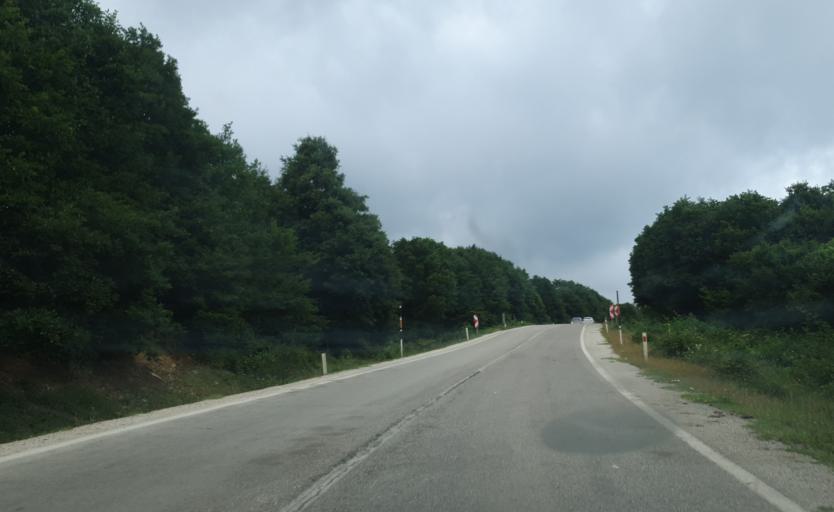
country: TR
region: Kirklareli
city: Salmydessus
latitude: 41.5650
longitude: 28.0704
